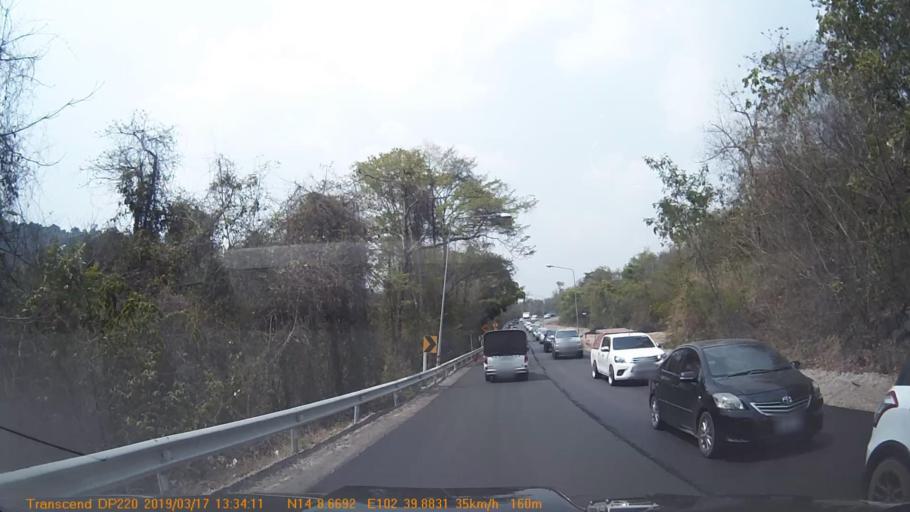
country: TH
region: Buriram
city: Non Din Daeng
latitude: 14.1446
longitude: 102.6646
